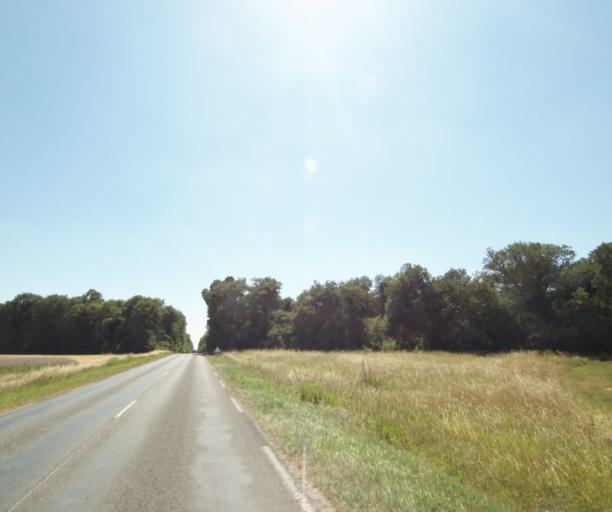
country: FR
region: Centre
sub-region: Departement du Loiret
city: Malesherbes
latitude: 48.3174
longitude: 2.4414
